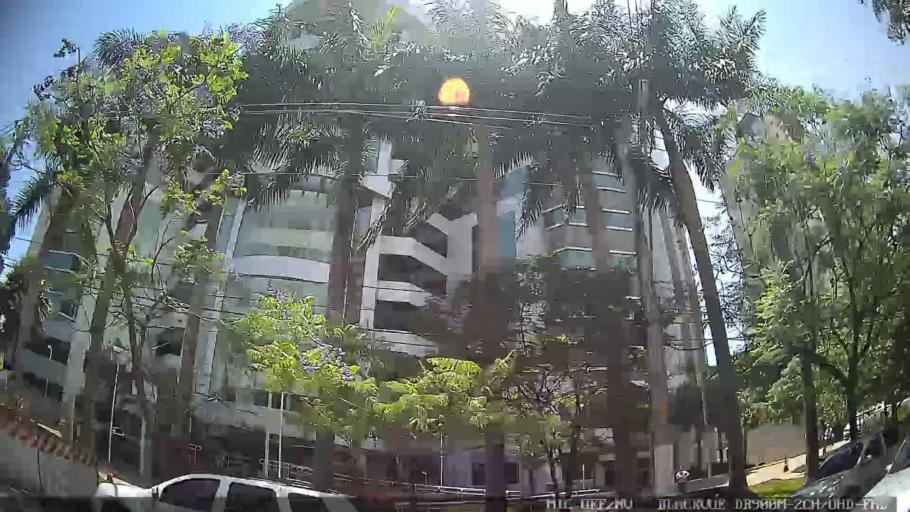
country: BR
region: Sao Paulo
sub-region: Sao Caetano Do Sul
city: Sao Caetano do Sul
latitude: -23.5637
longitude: -46.5615
